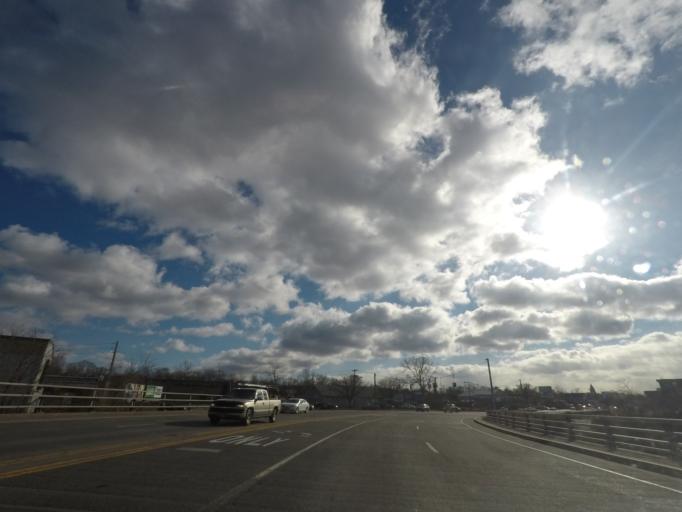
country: US
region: New York
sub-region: Schenectady County
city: Schenectady
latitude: 42.8293
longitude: -73.9300
